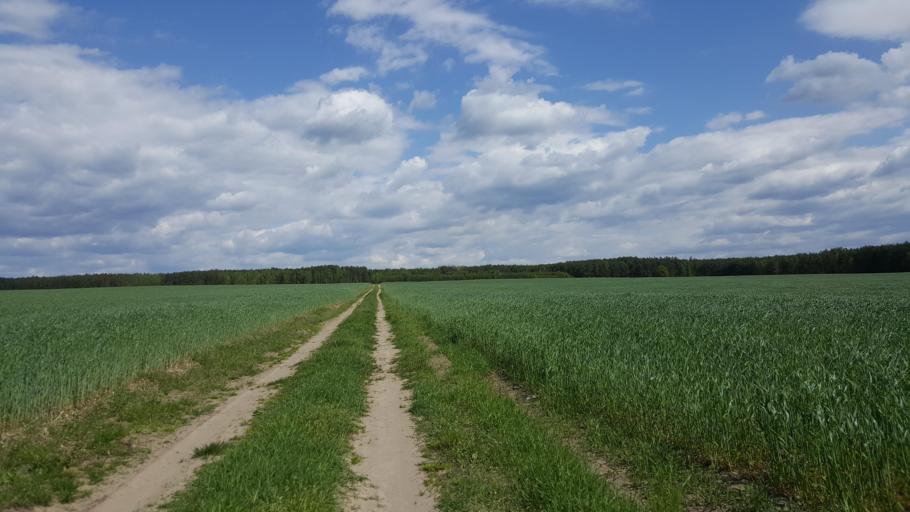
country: BY
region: Brest
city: Kamyanyets
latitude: 52.3773
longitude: 23.9273
